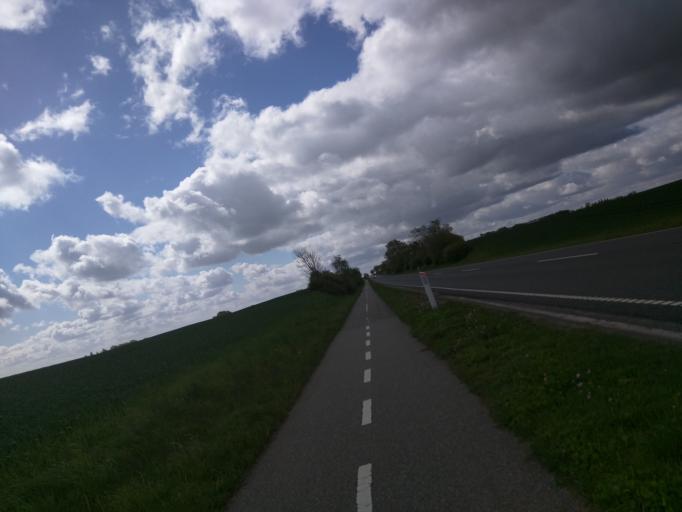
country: DK
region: Central Jutland
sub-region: Silkeborg Kommune
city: Kjellerup
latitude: 56.3150
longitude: 9.4214
